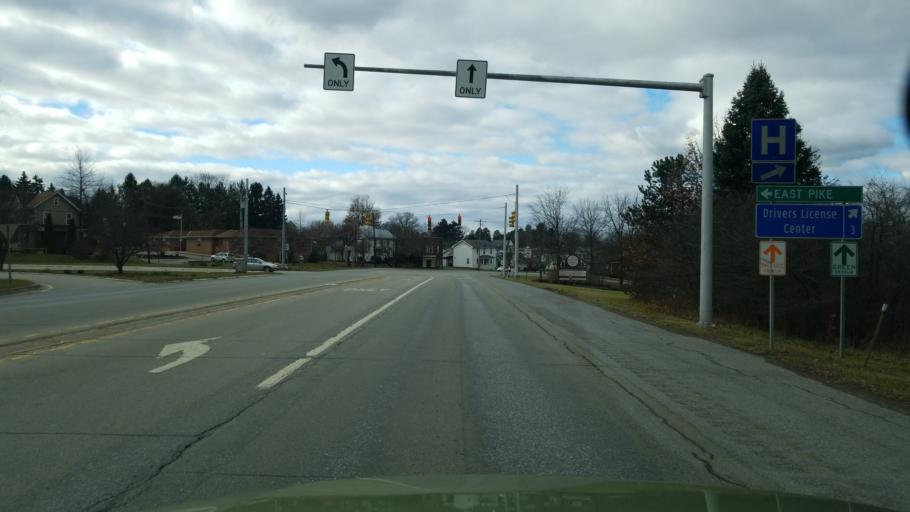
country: US
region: Pennsylvania
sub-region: Indiana County
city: Chevy Chase Heights
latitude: 40.6235
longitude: -79.1379
